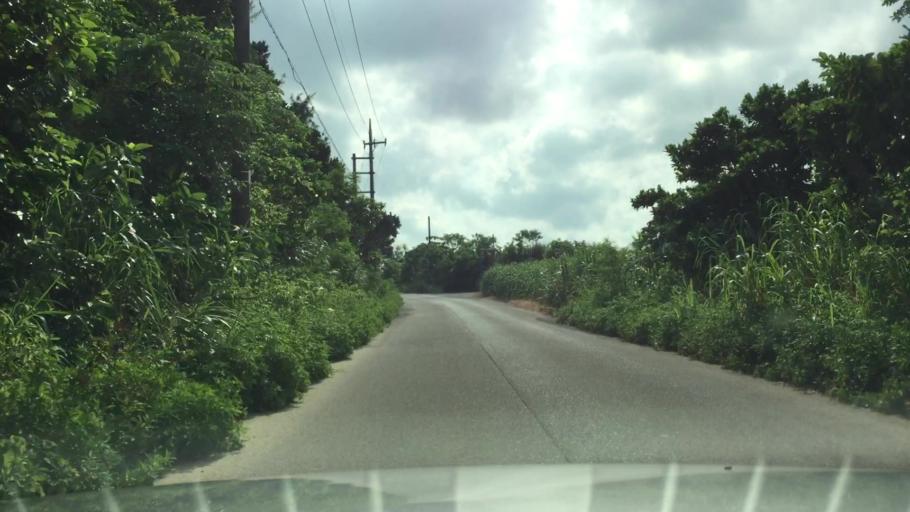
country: JP
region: Okinawa
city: Ishigaki
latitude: 24.4000
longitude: 124.2057
